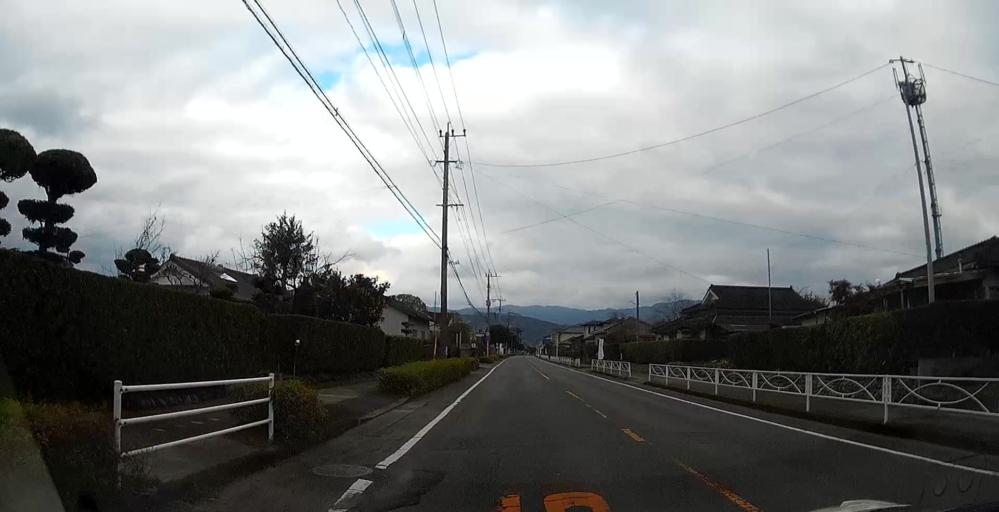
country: JP
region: Kagoshima
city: Izumi
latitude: 32.0753
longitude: 130.3494
